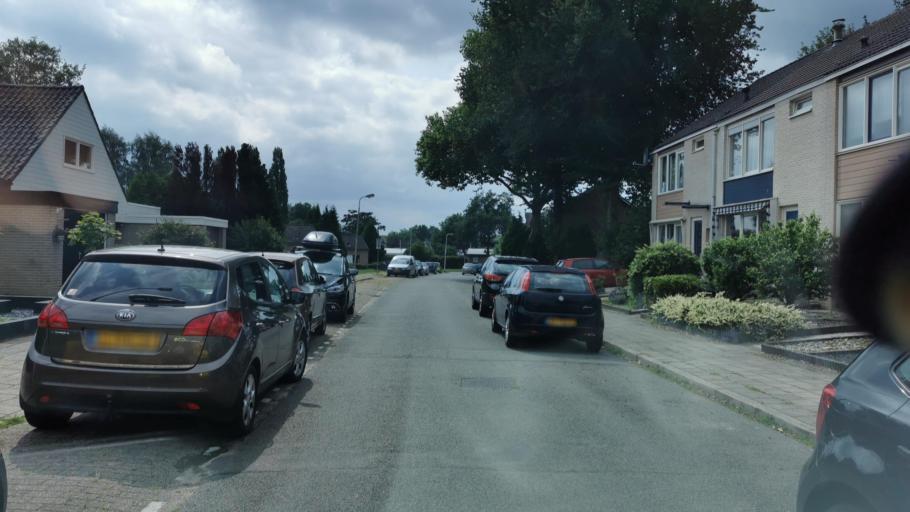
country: NL
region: Overijssel
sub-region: Gemeente Losser
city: Losser
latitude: 52.2566
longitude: 7.0058
